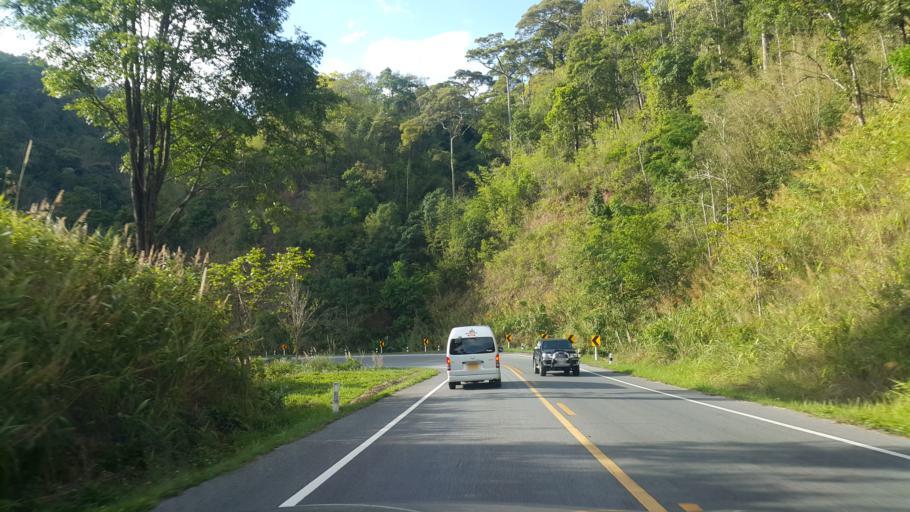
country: TH
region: Phayao
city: Phayao
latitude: 19.0719
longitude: 99.7727
